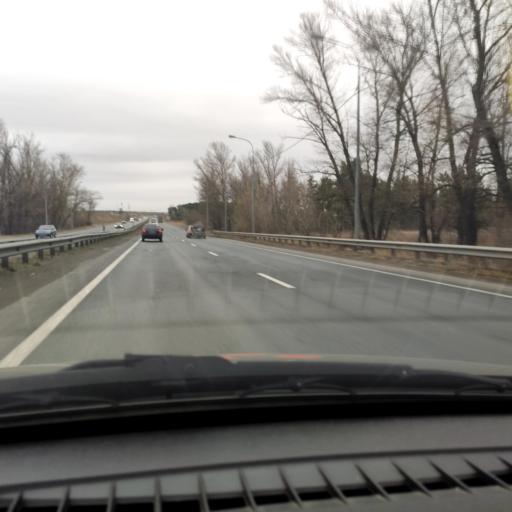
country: RU
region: Samara
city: Zhigulevsk
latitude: 53.5290
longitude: 49.5213
